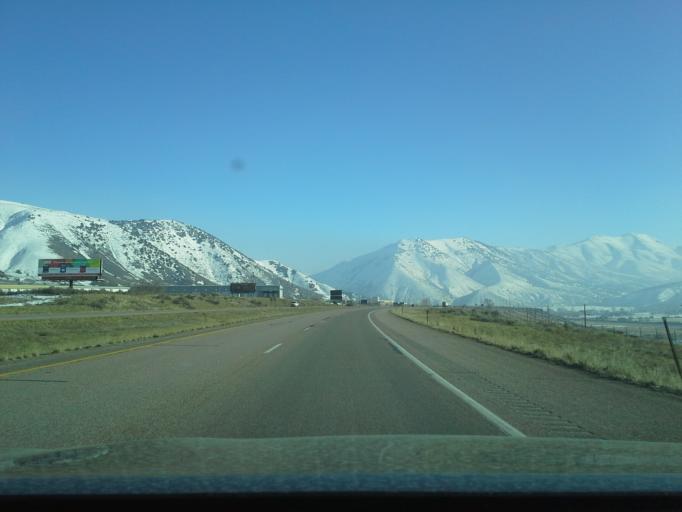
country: US
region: Idaho
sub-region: Bannock County
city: Pocatello
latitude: 42.8164
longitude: -112.3838
